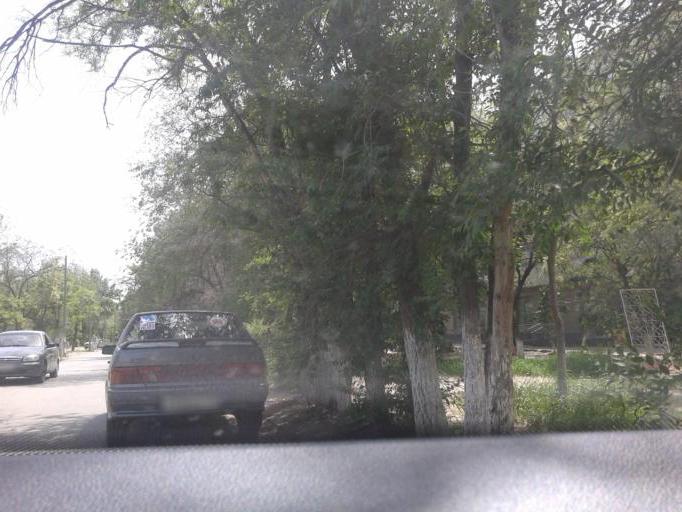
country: RU
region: Volgograd
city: Volgograd
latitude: 48.6081
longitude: 44.4215
